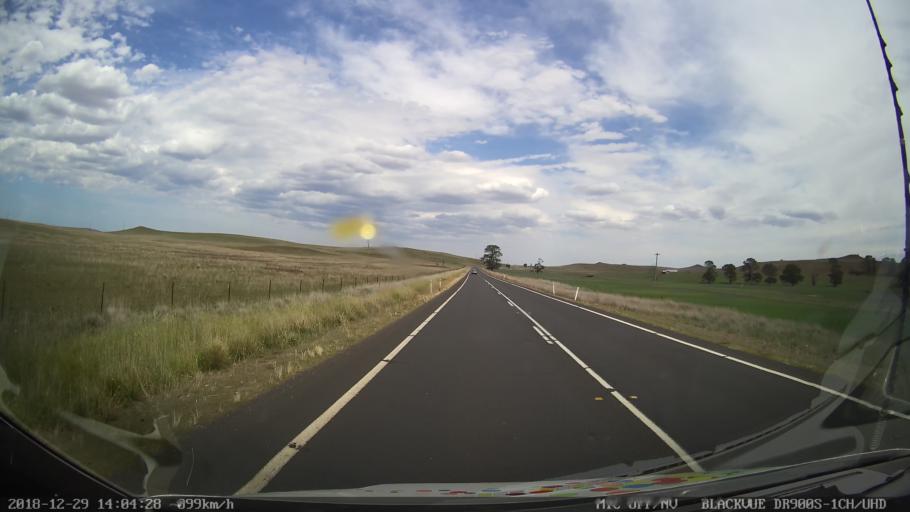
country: AU
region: New South Wales
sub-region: Cooma-Monaro
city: Cooma
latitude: -36.3165
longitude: 149.1868
